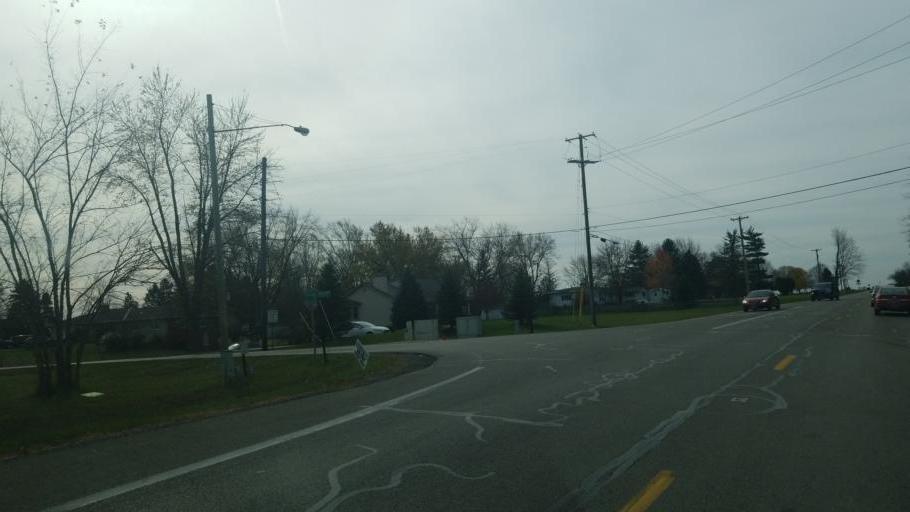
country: US
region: Ohio
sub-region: Madison County
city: London
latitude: 39.9226
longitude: -83.4137
